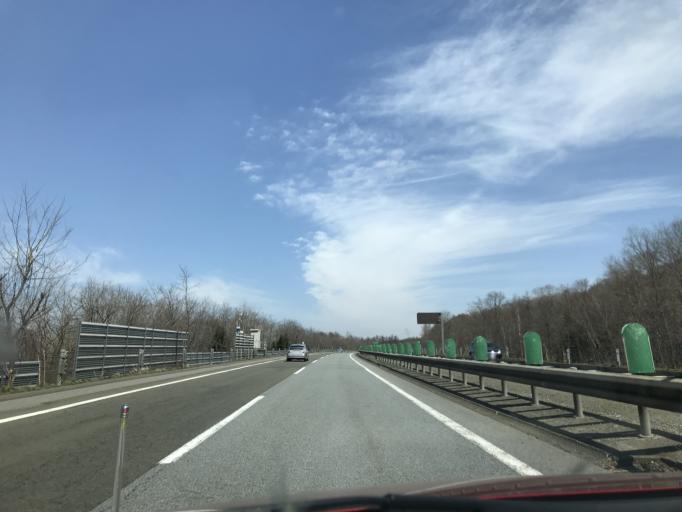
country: JP
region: Hokkaido
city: Bibai
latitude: 43.2914
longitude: 141.8651
